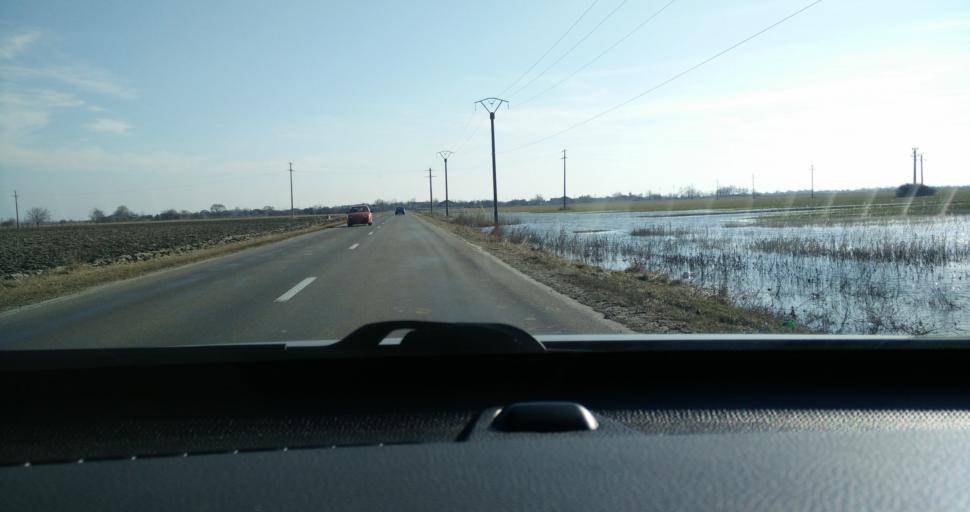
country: RO
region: Vrancea
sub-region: Comuna Nanesti
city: Nanesti
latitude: 45.5598
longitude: 27.4998
